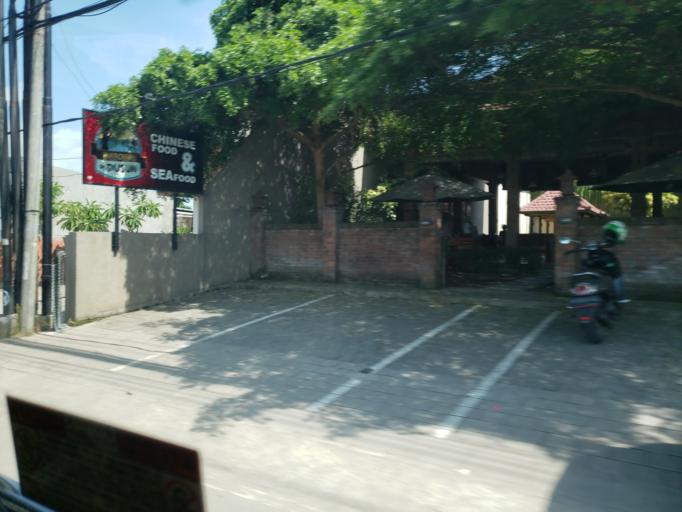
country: ID
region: Bali
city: Kangin
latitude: -8.8215
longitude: 115.1450
